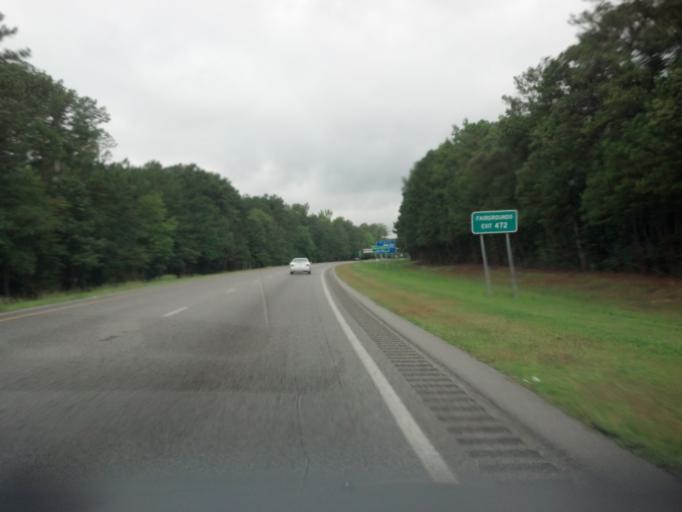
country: US
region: North Carolina
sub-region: Nash County
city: Rocky Mount
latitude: 35.9379
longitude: -77.7503
